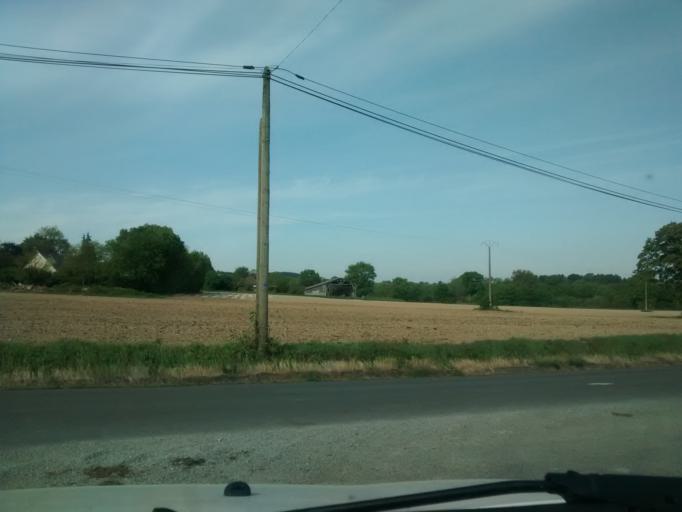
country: FR
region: Brittany
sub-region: Departement d'Ille-et-Vilaine
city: La Dominelais
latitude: 47.7926
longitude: -1.7170
